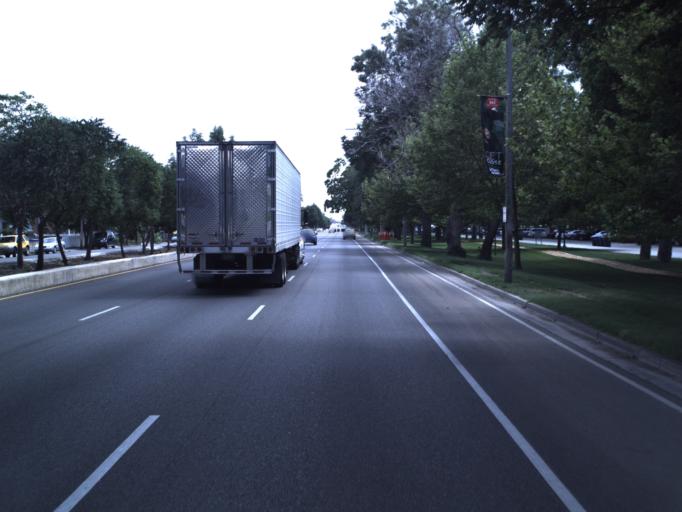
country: US
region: Utah
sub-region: Salt Lake County
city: Salt Lake City
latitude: 40.7482
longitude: -111.8713
